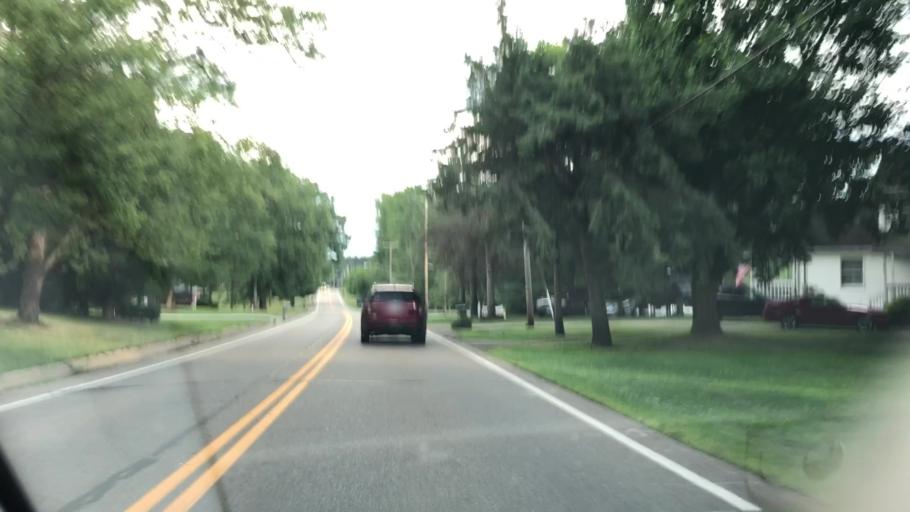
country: US
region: Ohio
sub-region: Summit County
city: Green
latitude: 40.9454
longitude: -81.4895
